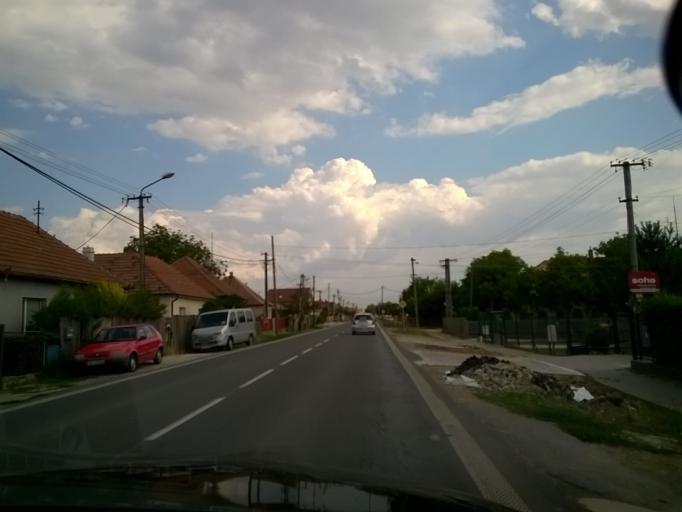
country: SK
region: Nitriansky
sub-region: Okres Nitra
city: Nitra
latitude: 48.3539
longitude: 18.0531
